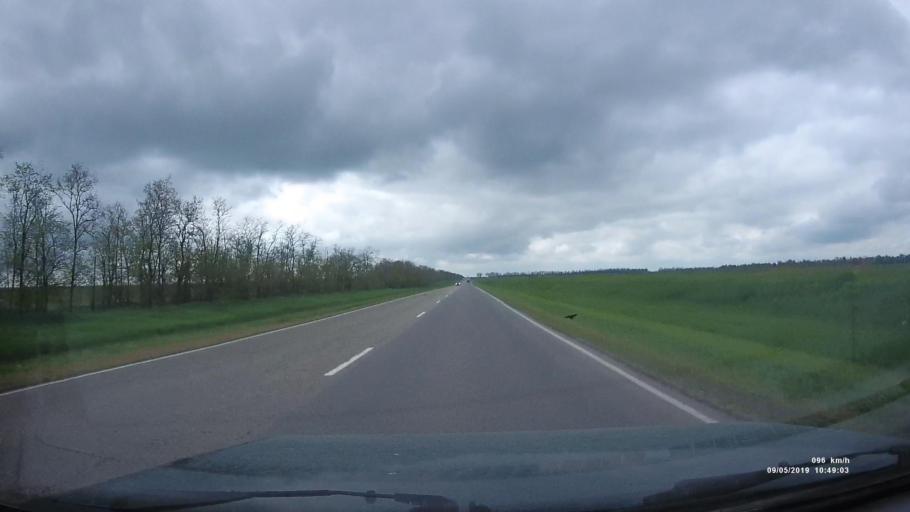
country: RU
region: Rostov
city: Peshkovo
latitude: 46.9481
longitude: 39.3562
